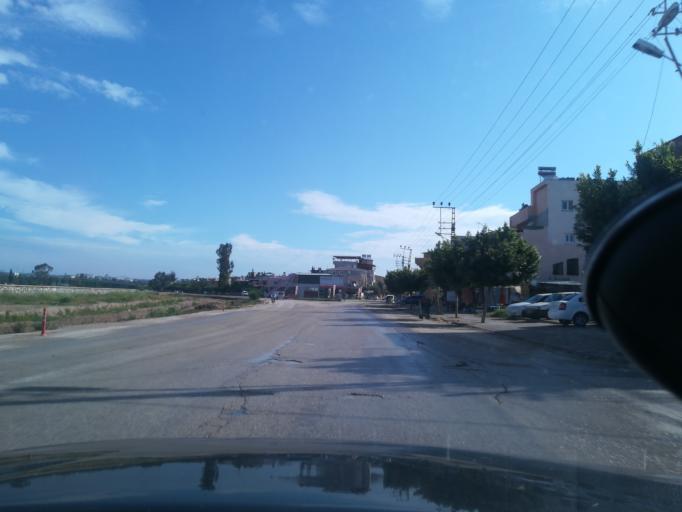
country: TR
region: Adana
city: Adana
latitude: 37.0155
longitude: 35.3620
